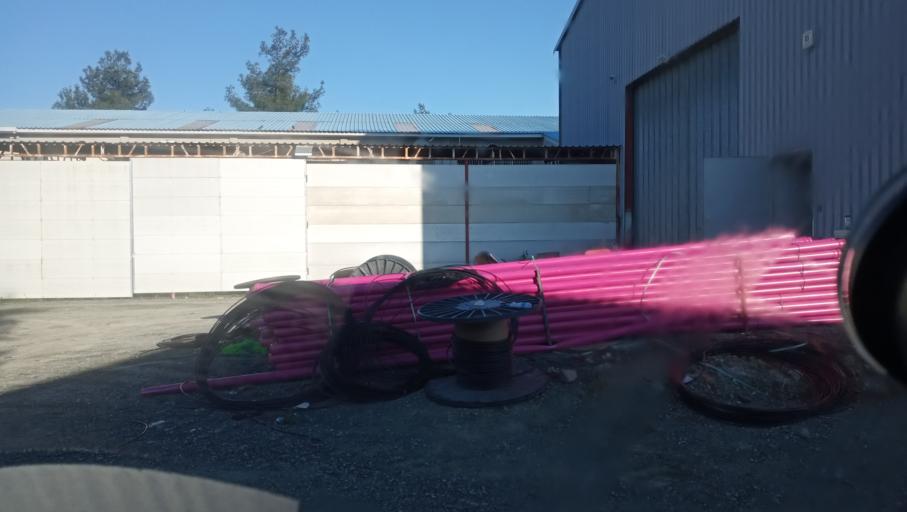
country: CY
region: Lefkosia
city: Nicosia
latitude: 35.1259
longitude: 33.3602
